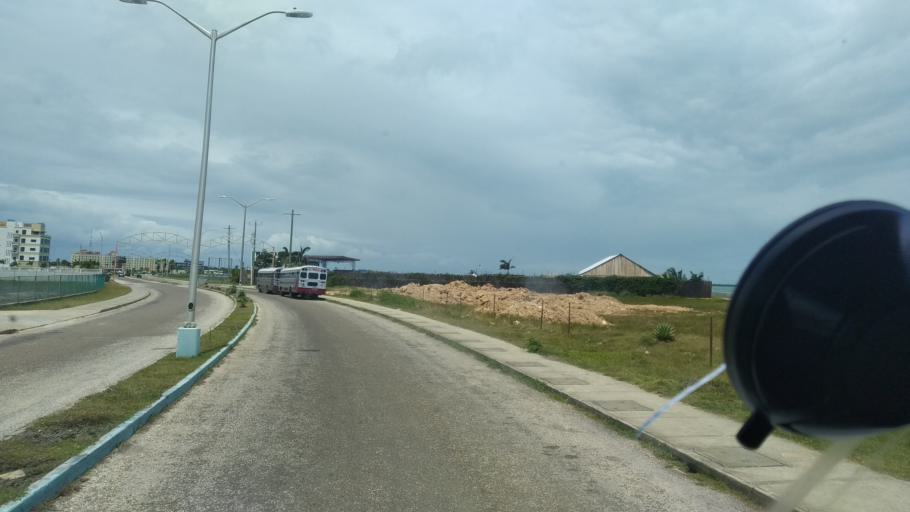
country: BZ
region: Belize
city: Belize City
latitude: 17.4979
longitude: -88.1816
